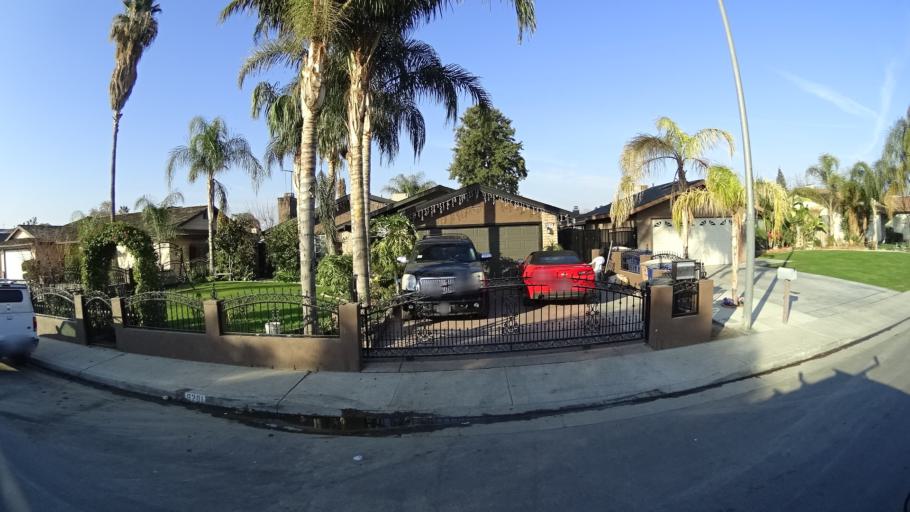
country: US
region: California
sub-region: Kern County
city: Greenfield
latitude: 35.2986
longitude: -119.0227
